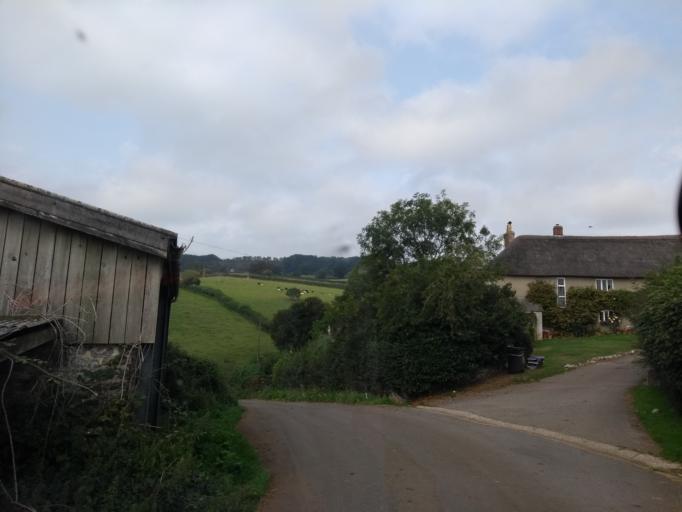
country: GB
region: England
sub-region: Somerset
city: Chard
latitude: 50.8752
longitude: -3.0701
